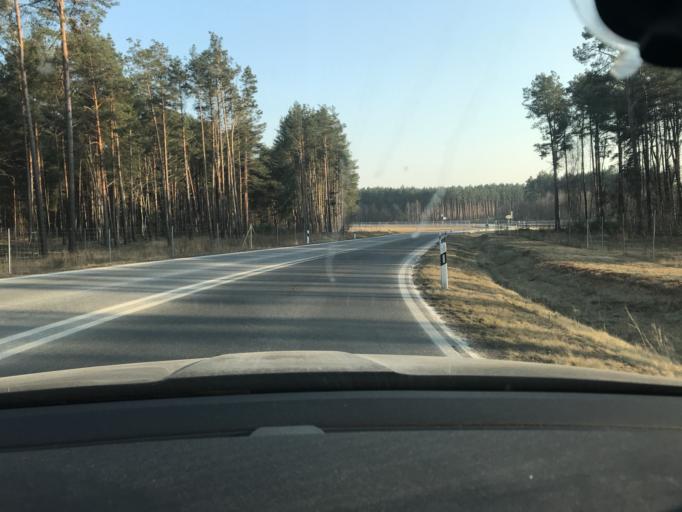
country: DE
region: Brandenburg
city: Erkner
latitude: 52.3216
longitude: 13.7797
